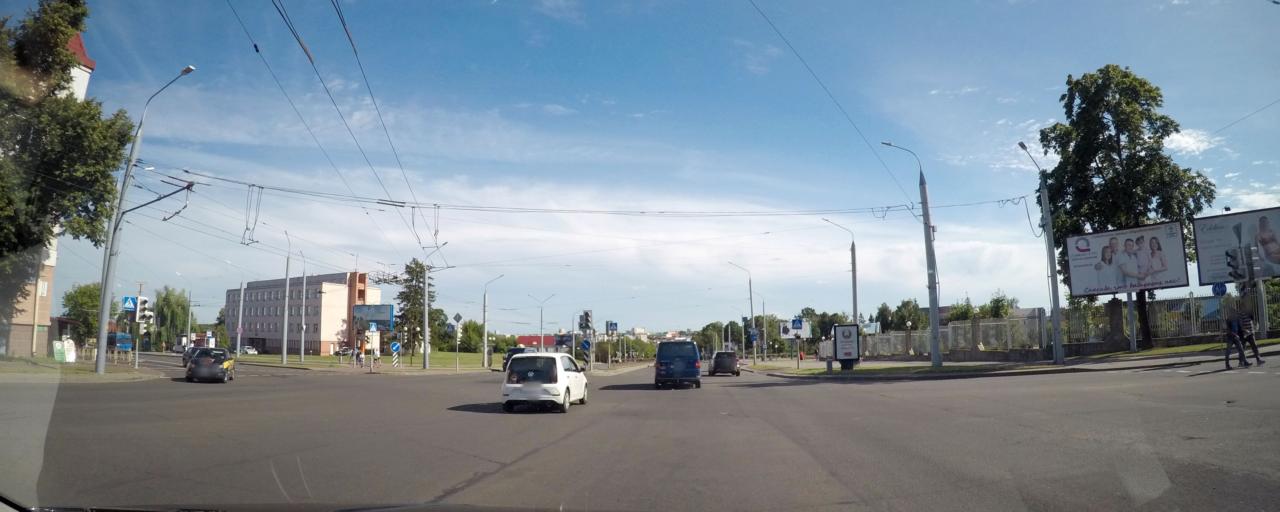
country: BY
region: Grodnenskaya
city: Hrodna
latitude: 53.6904
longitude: 23.8253
